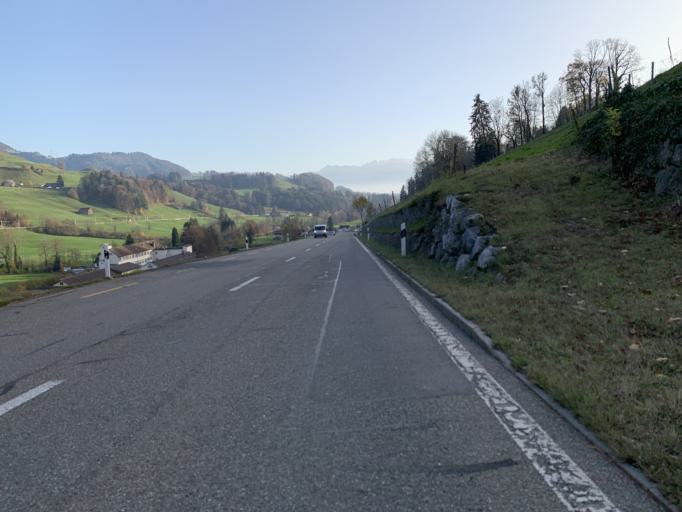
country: CH
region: Zurich
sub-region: Bezirk Hinwil
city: Wald
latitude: 47.3053
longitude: 8.9130
